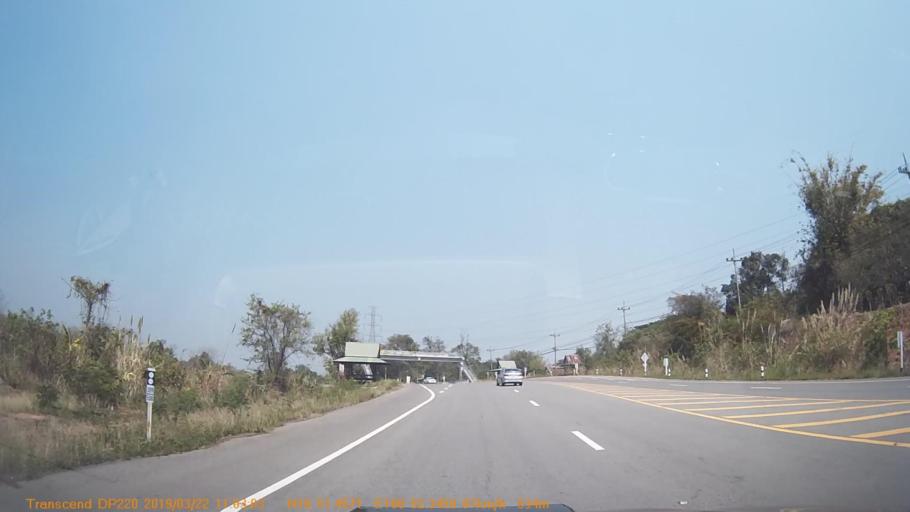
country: TH
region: Phitsanulok
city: Nakhon Thai
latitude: 16.8580
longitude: 100.8723
